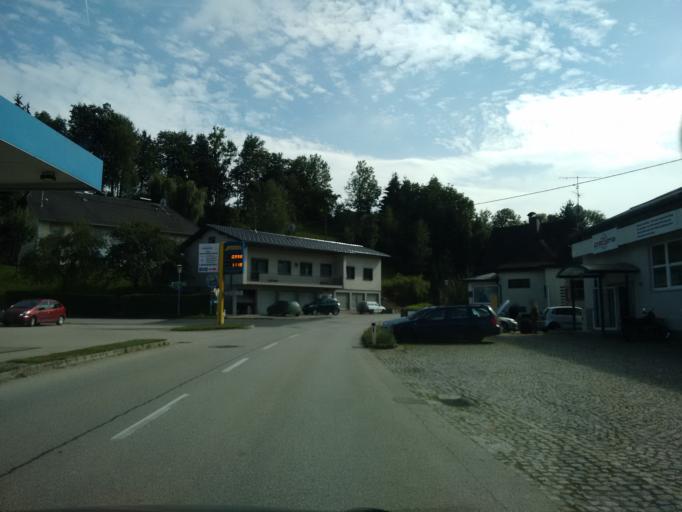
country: AT
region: Upper Austria
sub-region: Wels-Land
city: Marchtrenk
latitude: 48.1239
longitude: 14.0935
